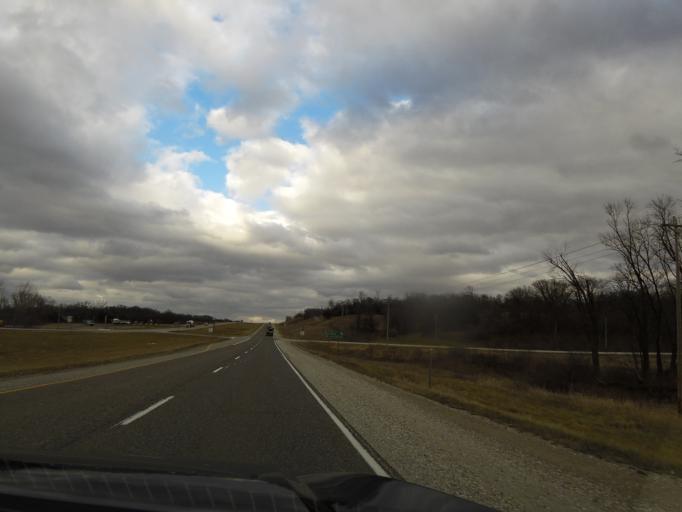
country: US
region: Iowa
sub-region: Henry County
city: Mount Pleasant
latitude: 40.8997
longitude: -91.5534
